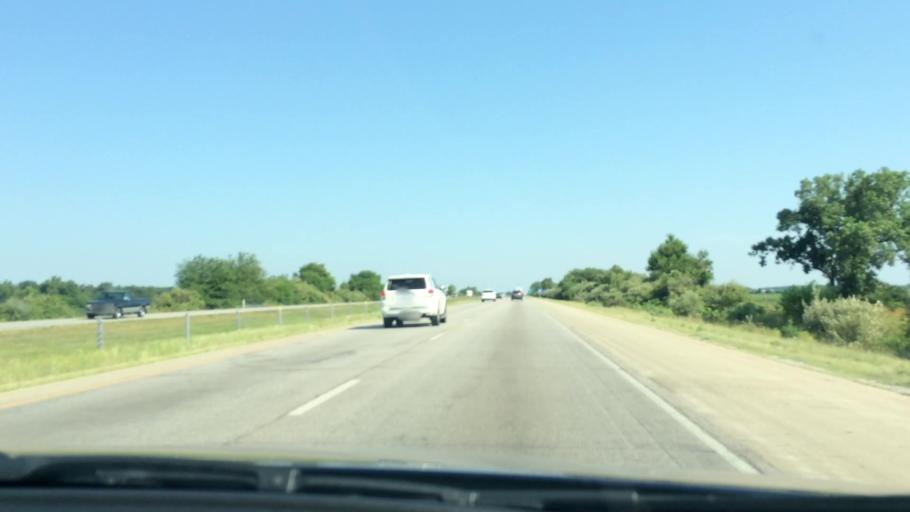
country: US
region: Indiana
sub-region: Jasper County
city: Rensselaer
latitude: 40.9861
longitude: -87.2576
